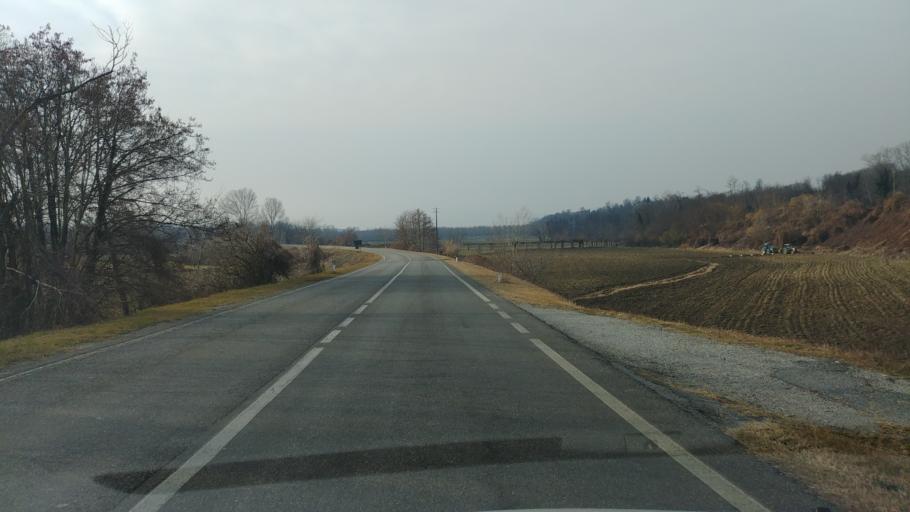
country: IT
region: Piedmont
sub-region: Provincia di Cuneo
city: Castelletto Stura
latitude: 44.4585
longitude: 7.6356
